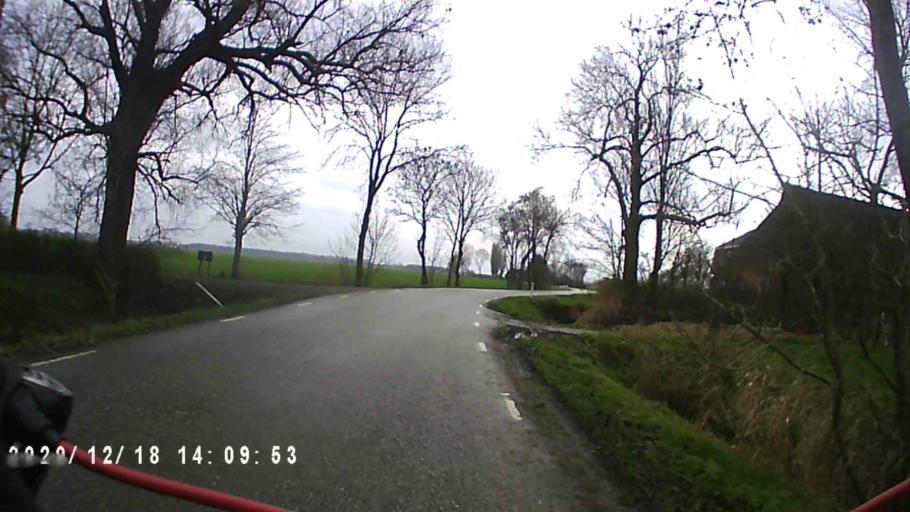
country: NL
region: Groningen
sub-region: Gemeente Bedum
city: Bedum
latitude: 53.2783
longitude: 6.6588
